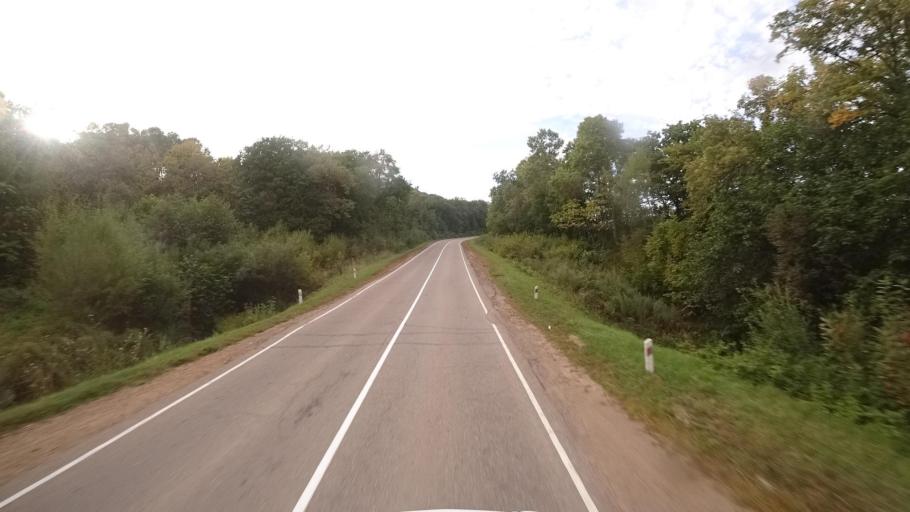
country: RU
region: Primorskiy
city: Yakovlevka
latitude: 44.4010
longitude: 133.4648
